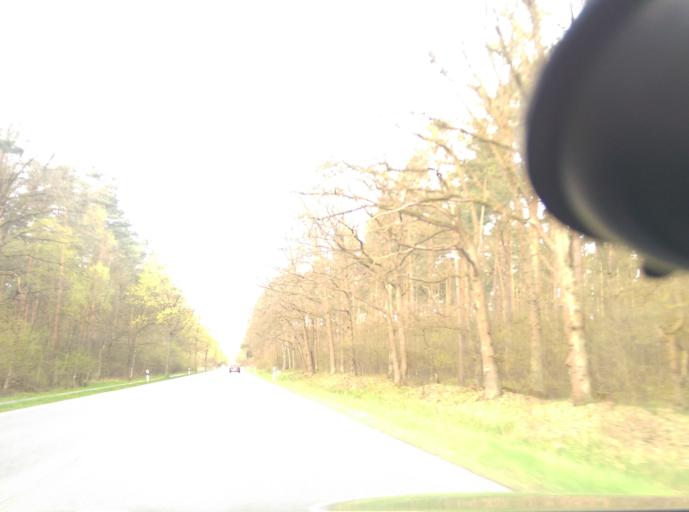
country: DE
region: Lower Saxony
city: Hambuhren
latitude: 52.6241
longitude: 10.0227
